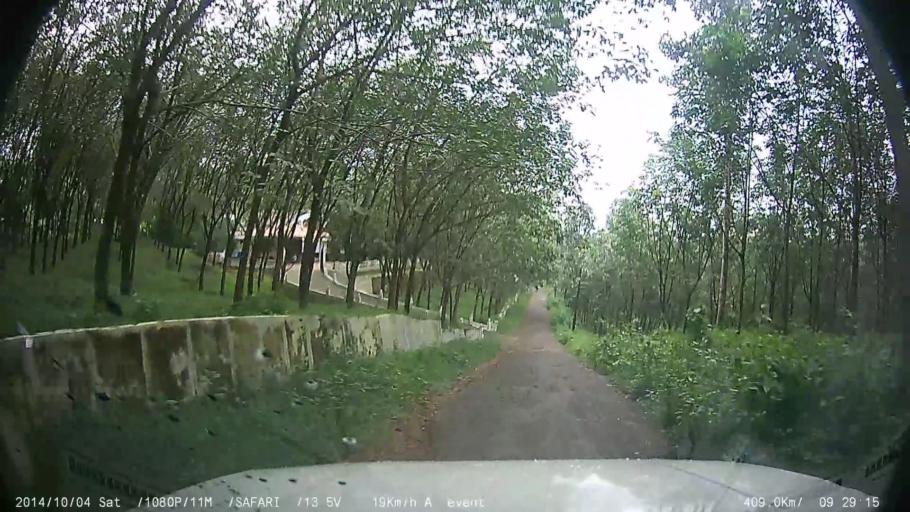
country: IN
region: Kerala
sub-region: Kottayam
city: Palackattumala
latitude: 9.7862
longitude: 76.5740
